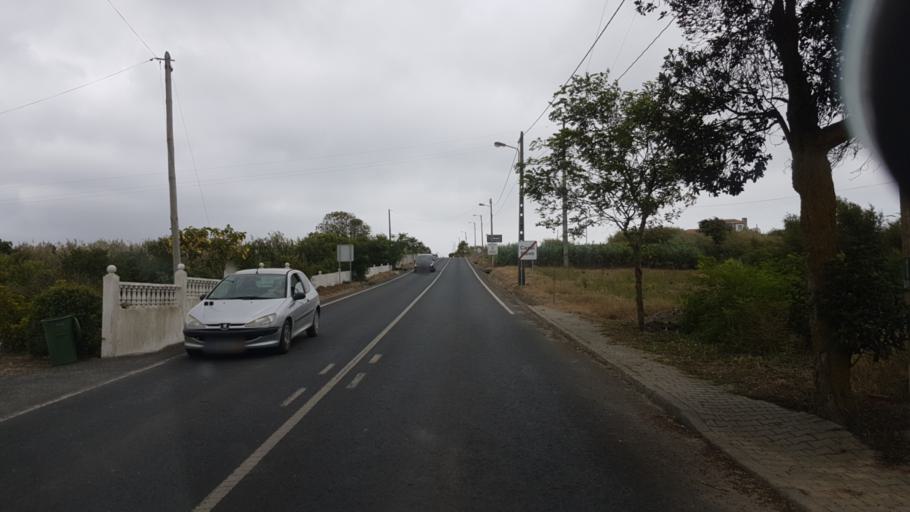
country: PT
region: Lisbon
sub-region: Lourinha
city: Lourinha
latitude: 39.2187
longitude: -9.3206
